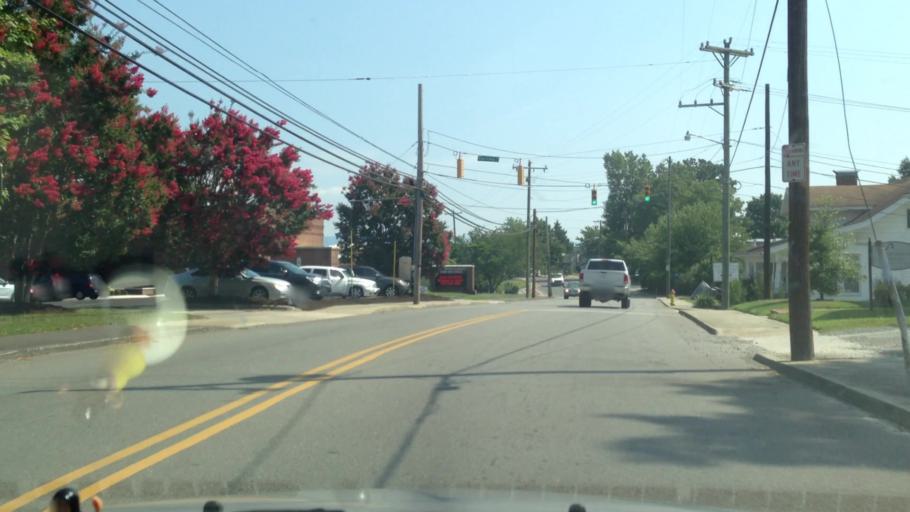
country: US
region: North Carolina
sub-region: Surry County
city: Mount Airy
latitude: 36.4971
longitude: -80.6091
